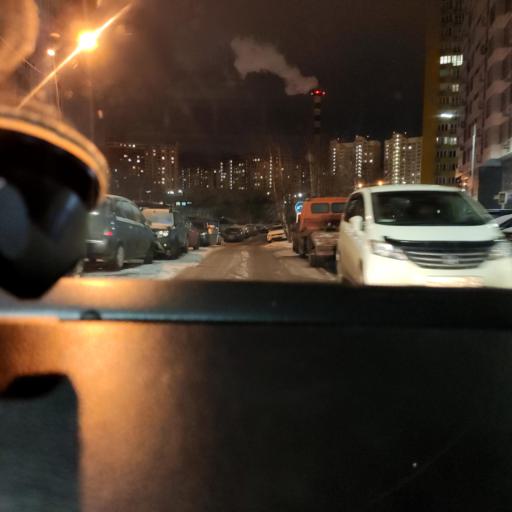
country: RU
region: Moskovskaya
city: Vidnoye
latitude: 55.5424
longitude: 37.7140
